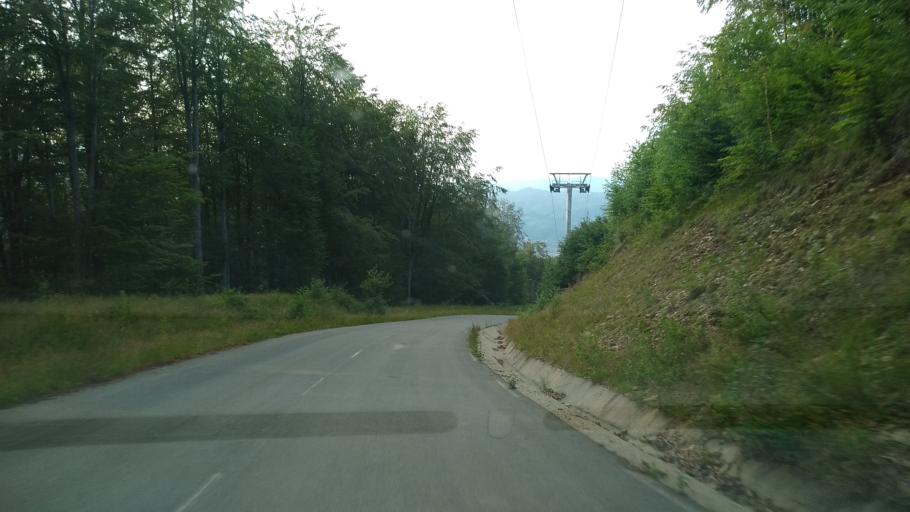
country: RO
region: Hunedoara
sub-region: Municipiul  Vulcan
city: Jiu-Paroseni
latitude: 45.3386
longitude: 23.2911
